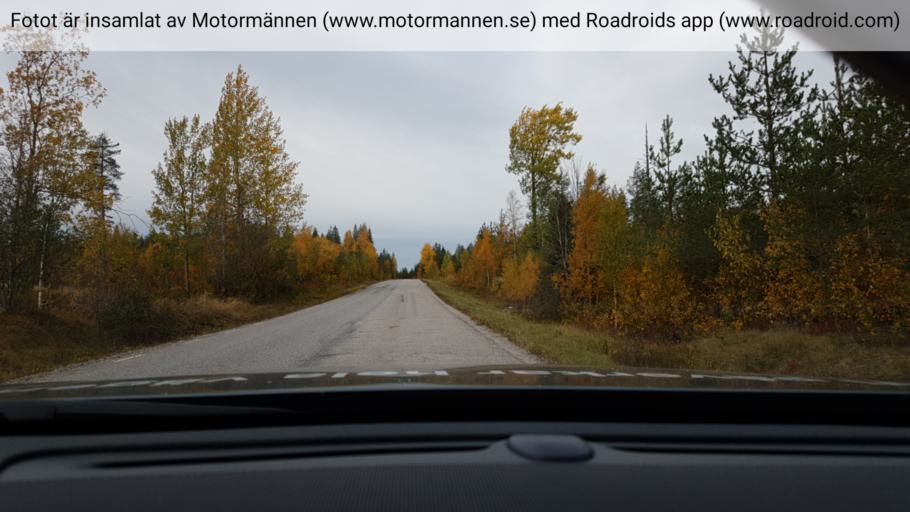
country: SE
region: Norrbotten
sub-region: Overkalix Kommun
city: OEverkalix
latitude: 66.2581
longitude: 23.0642
